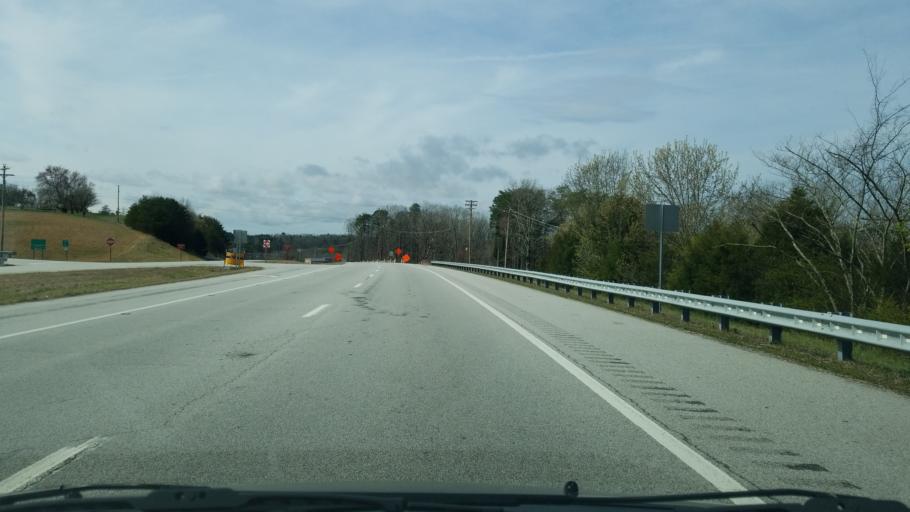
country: US
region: Tennessee
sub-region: Hamilton County
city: Lakesite
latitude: 35.1848
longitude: -85.0624
